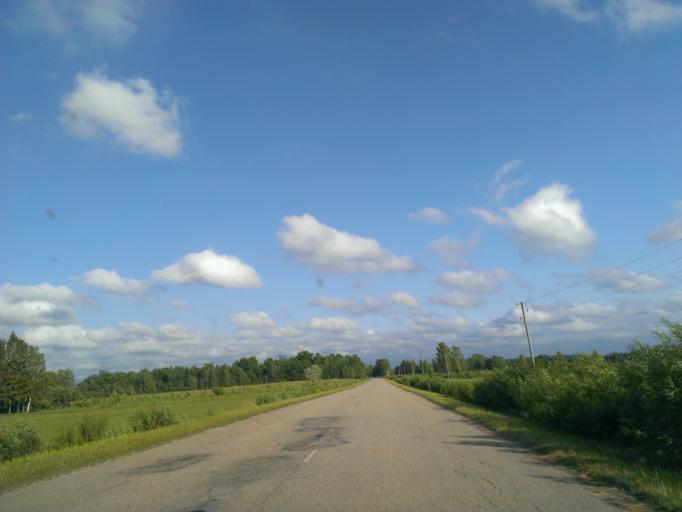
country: LV
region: Aizpute
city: Aizpute
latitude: 56.7956
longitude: 21.5024
